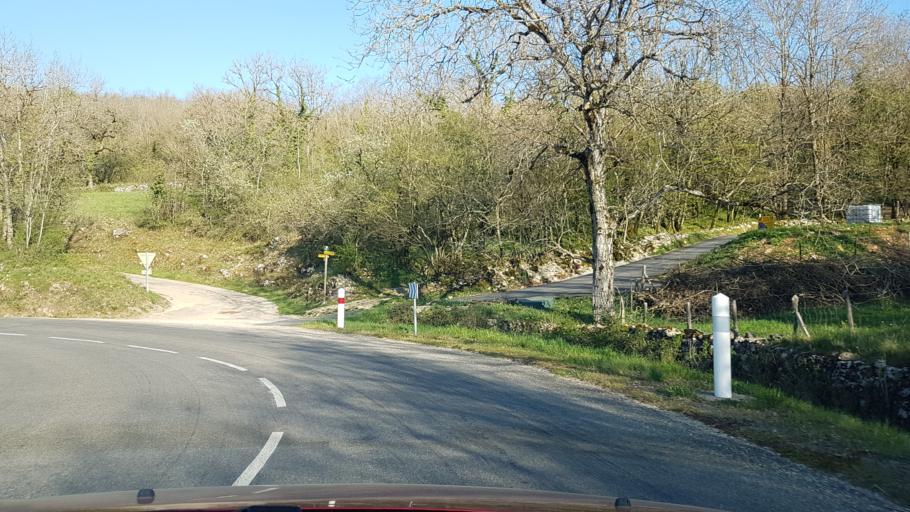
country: FR
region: Bourgogne
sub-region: Departement de Saone-et-Loire
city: Cuiseaux
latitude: 46.4611
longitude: 5.3873
